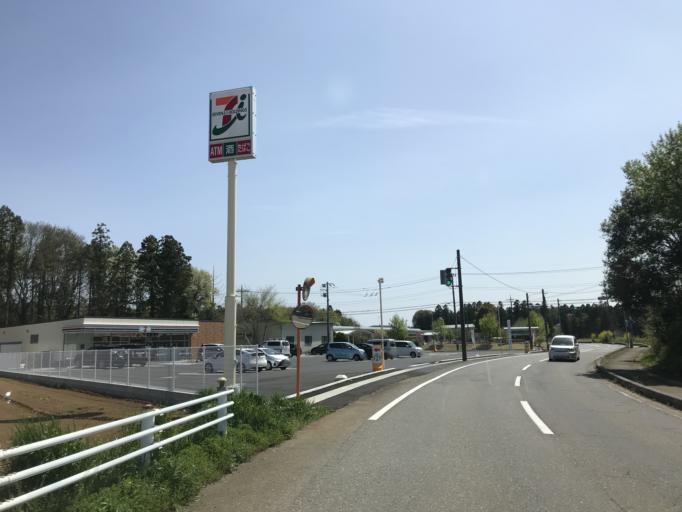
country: JP
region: Ibaraki
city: Naka
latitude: 36.0525
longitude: 140.0728
